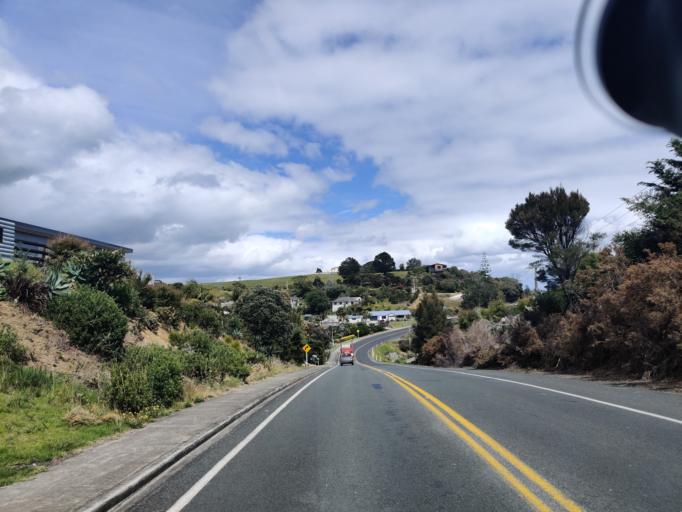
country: NZ
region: Northland
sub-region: Far North District
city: Taipa
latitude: -34.9929
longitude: 173.4944
